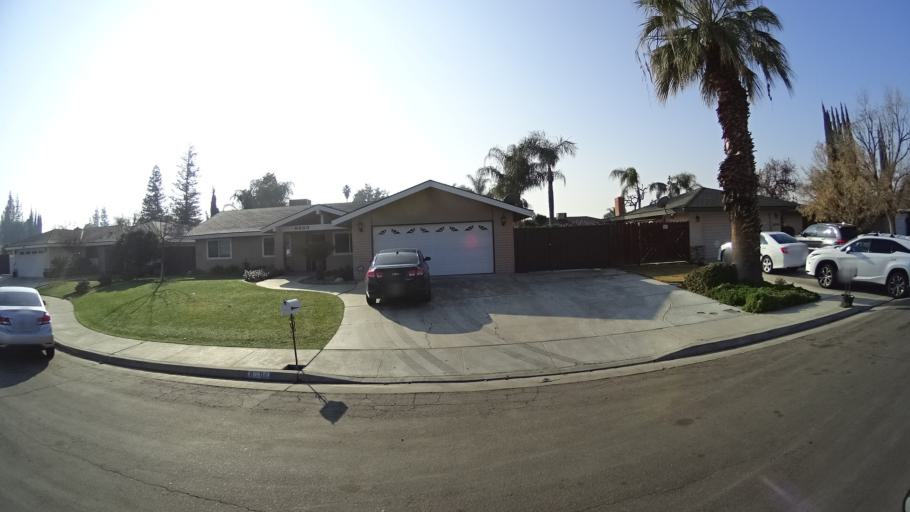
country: US
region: California
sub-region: Kern County
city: Greenacres
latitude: 35.3405
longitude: -119.0767
